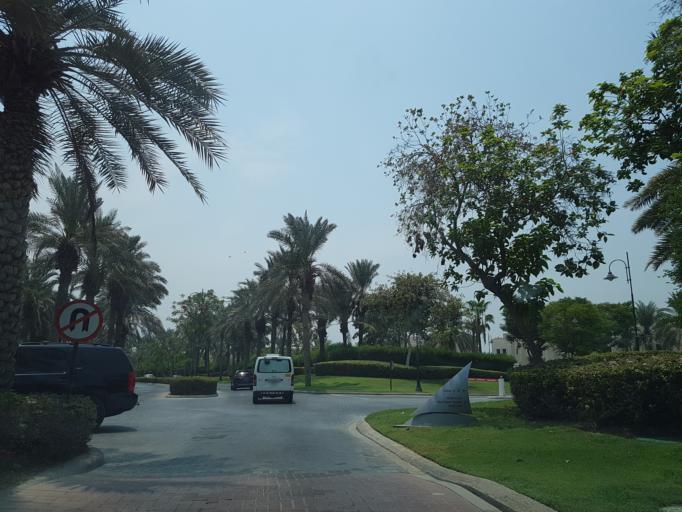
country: AE
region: Ash Shariqah
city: Sharjah
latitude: 25.2499
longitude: 55.3298
